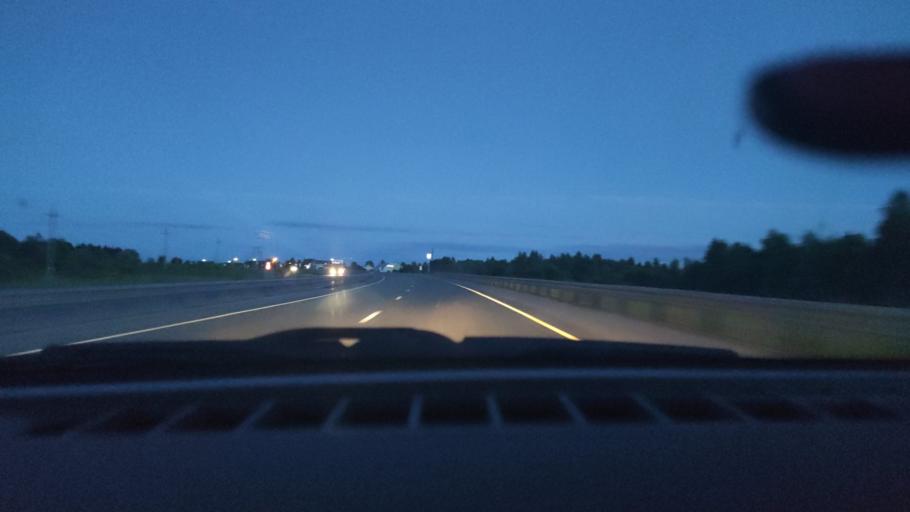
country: RU
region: Perm
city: Polazna
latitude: 58.1993
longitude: 56.4028
